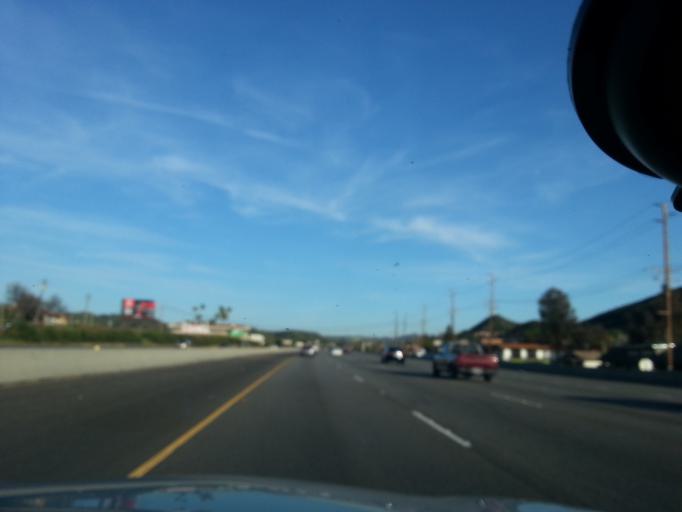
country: US
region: California
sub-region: Los Angeles County
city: Agoura
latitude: 34.1453
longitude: -118.7560
